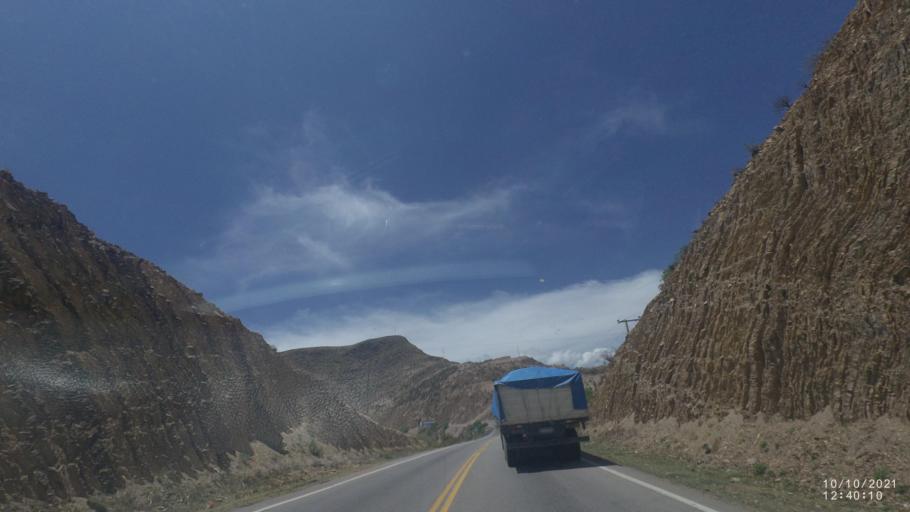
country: BO
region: Cochabamba
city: Irpa Irpa
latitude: -17.6418
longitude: -66.3909
